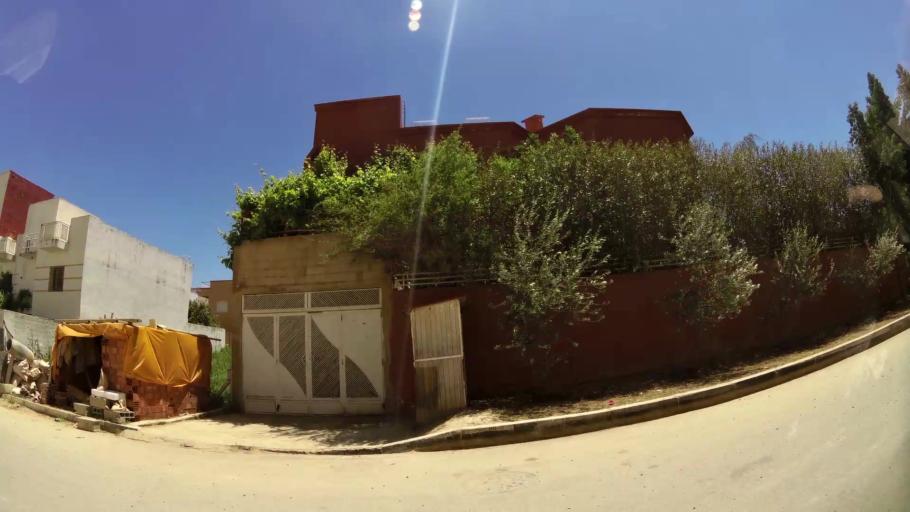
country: MA
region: Meknes-Tafilalet
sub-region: Meknes
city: Meknes
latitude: 33.8544
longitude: -5.5629
